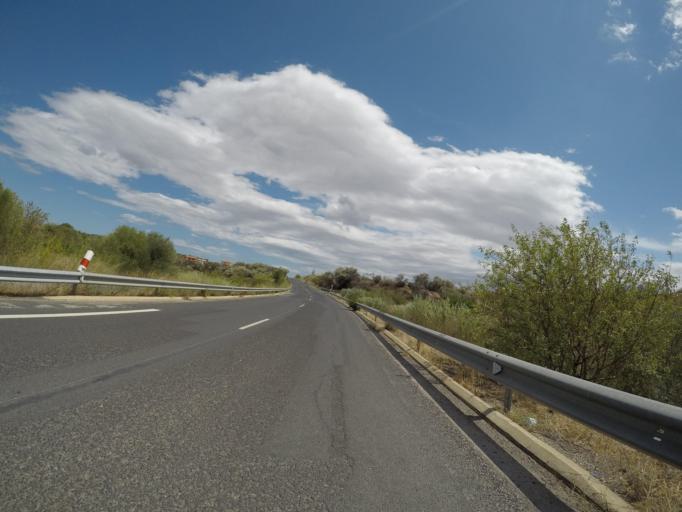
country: FR
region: Languedoc-Roussillon
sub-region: Departement des Pyrenees-Orientales
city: Baixas
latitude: 42.7455
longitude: 2.8073
